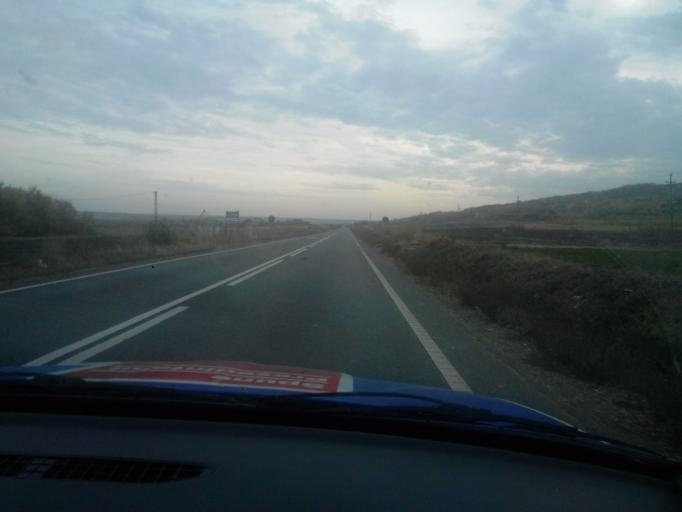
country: RO
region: Vaslui
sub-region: Comuna Tutova
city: Tutova
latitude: 46.1397
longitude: 27.5784
